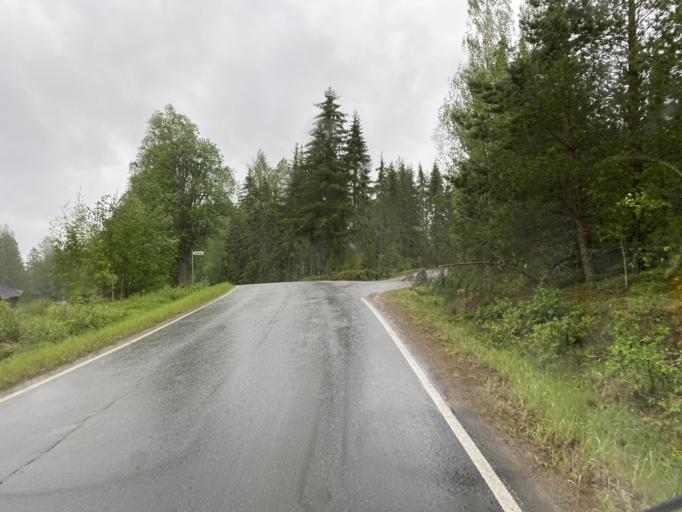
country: FI
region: Haeme
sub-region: Forssa
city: Humppila
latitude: 61.0728
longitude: 23.3125
